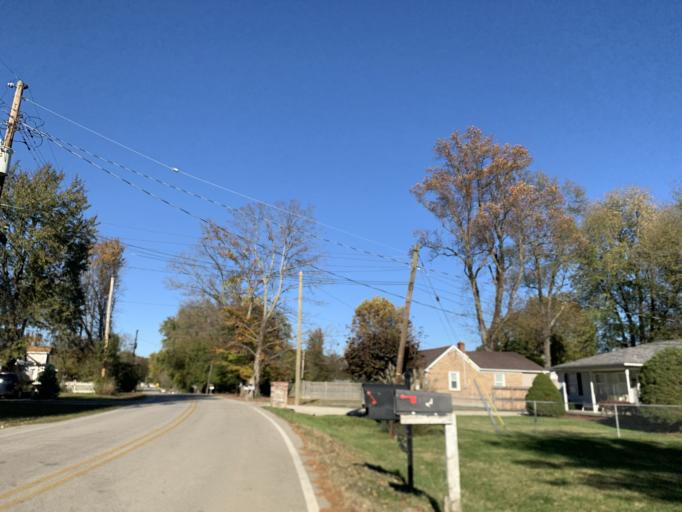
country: US
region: Kentucky
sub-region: Jefferson County
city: Pleasure Ridge Park
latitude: 38.1541
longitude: -85.8777
